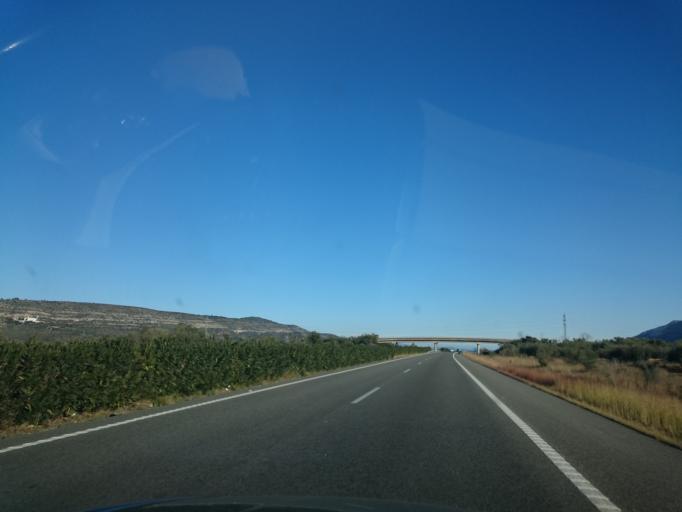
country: ES
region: Catalonia
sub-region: Provincia de Tarragona
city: Ulldecona
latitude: 40.6120
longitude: 0.4780
